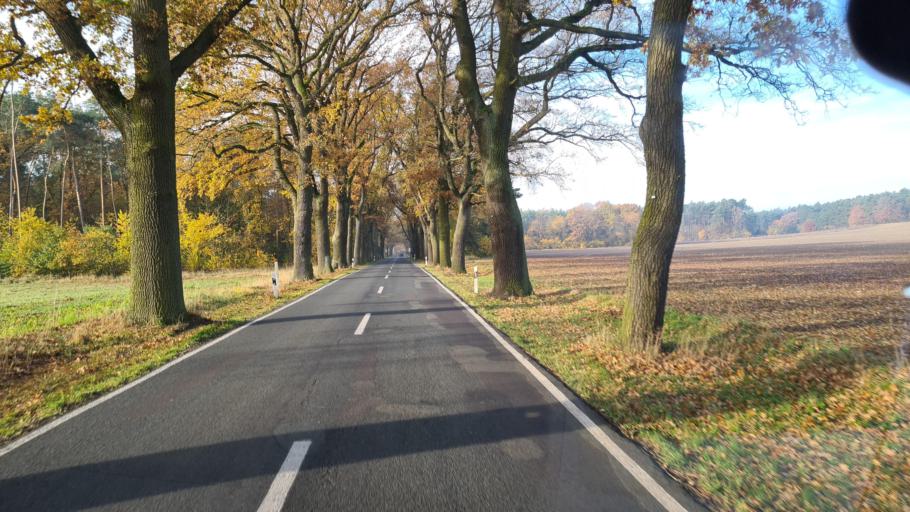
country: DE
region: Brandenburg
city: Golzow
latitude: 52.2836
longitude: 12.6481
